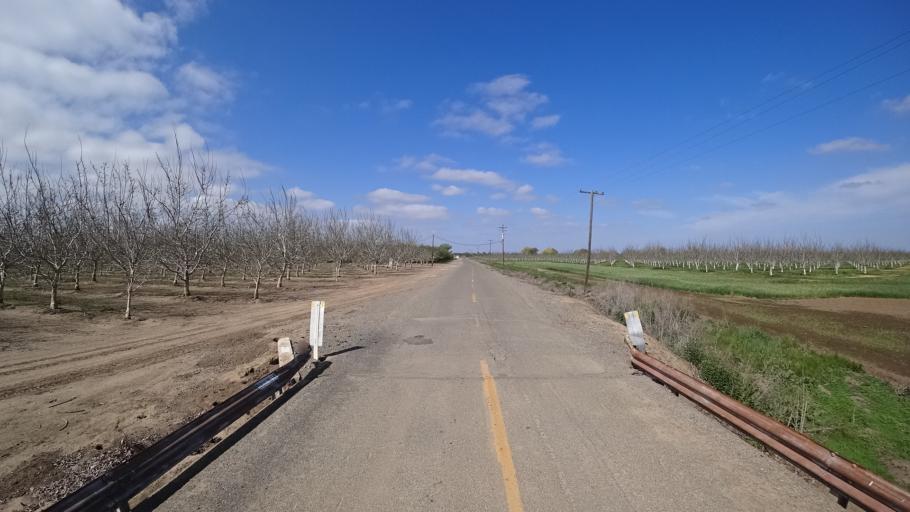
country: US
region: California
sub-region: Colusa County
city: Colusa
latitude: 39.4200
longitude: -121.9418
